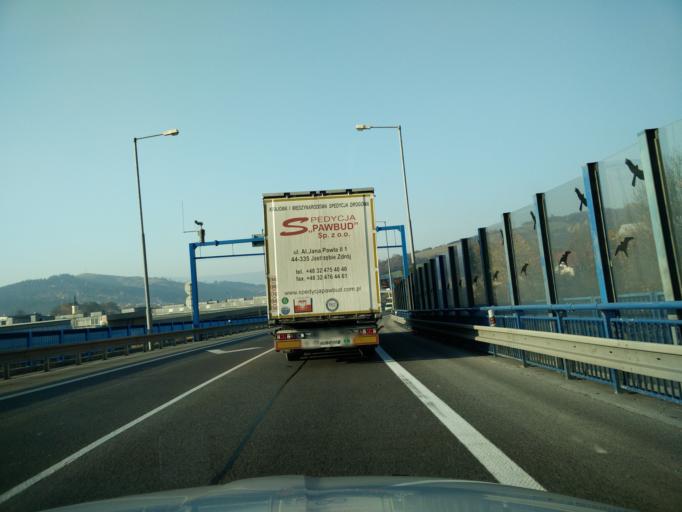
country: SK
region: Zilinsky
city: Cadca
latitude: 49.4343
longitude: 18.8004
